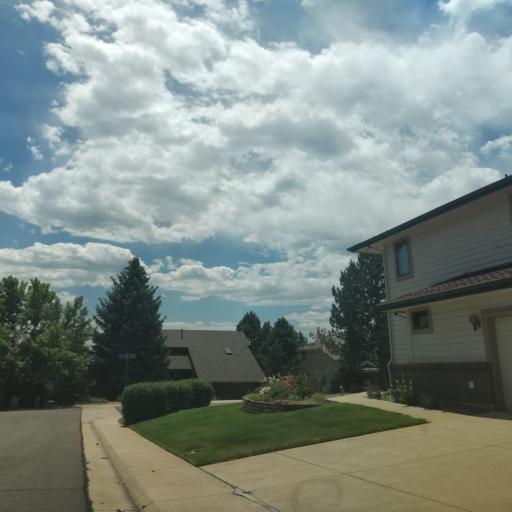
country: US
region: Colorado
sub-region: Jefferson County
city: Lakewood
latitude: 39.6748
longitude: -105.0956
